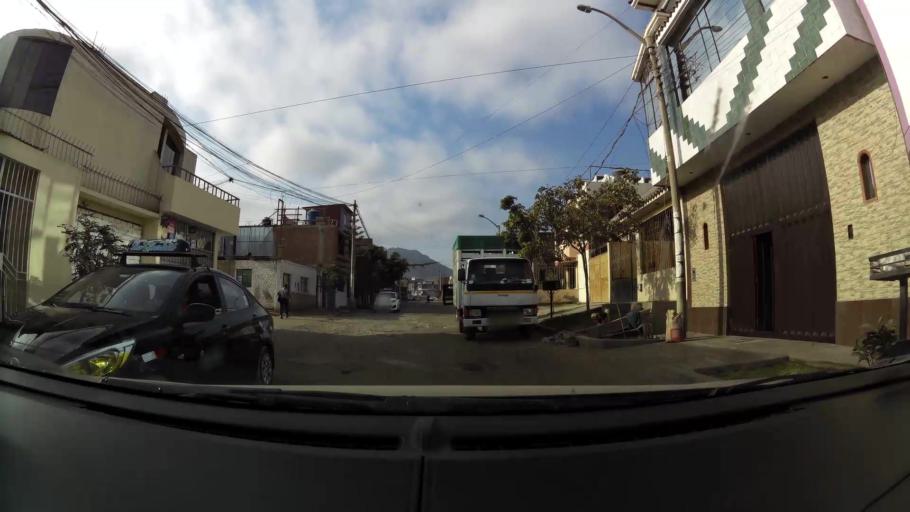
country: PE
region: La Libertad
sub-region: Provincia de Trujillo
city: La Esperanza
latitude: -8.0891
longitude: -79.0363
